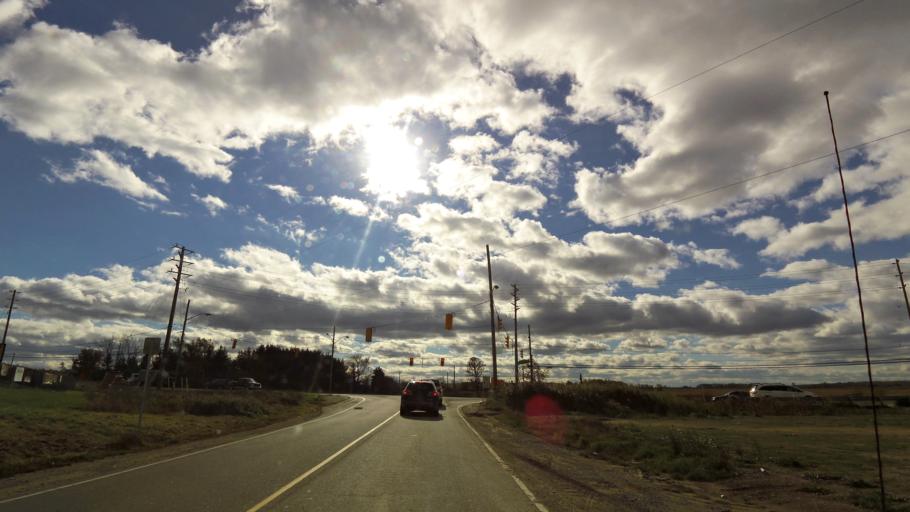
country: CA
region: Ontario
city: Burlington
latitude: 43.4672
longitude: -79.8077
